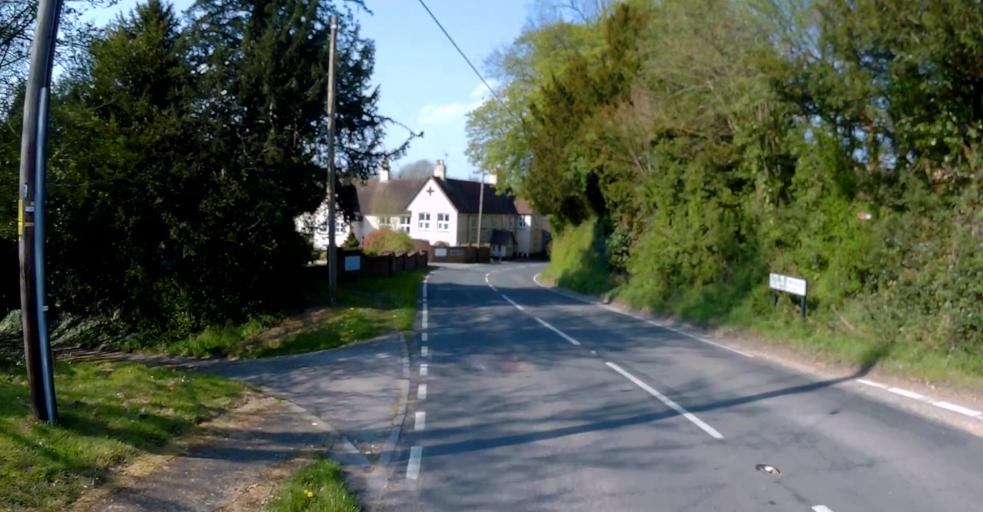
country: GB
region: England
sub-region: Hampshire
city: Four Marks
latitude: 51.0998
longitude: -1.1618
